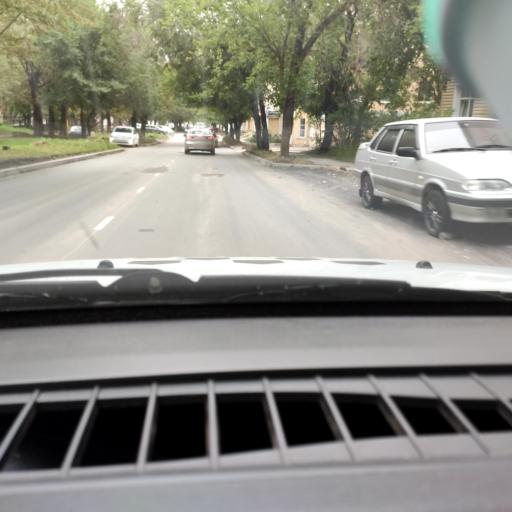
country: RU
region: Chelyabinsk
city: Miass
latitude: 55.0542
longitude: 60.1106
